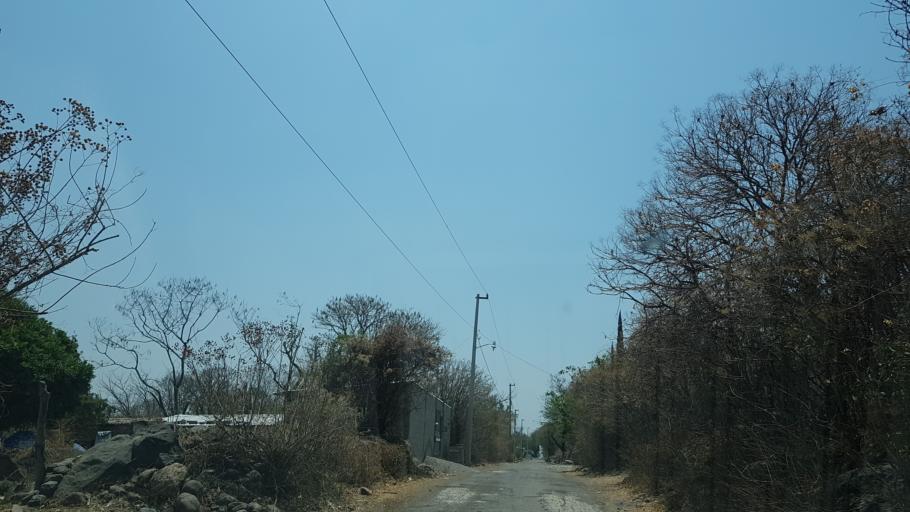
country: MX
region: Puebla
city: Huaquechula
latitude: 18.7793
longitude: -98.5446
